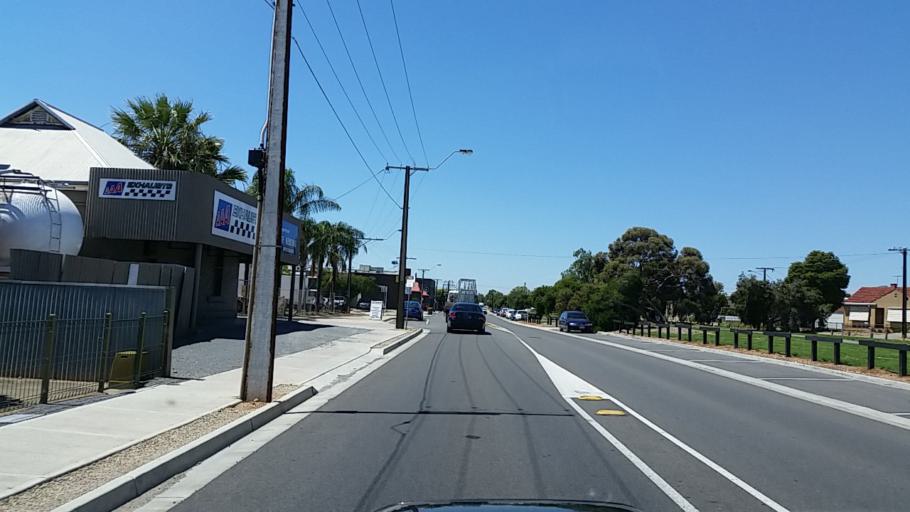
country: AU
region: South Australia
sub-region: Unley
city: Forestville
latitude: -34.9416
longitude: 138.5678
